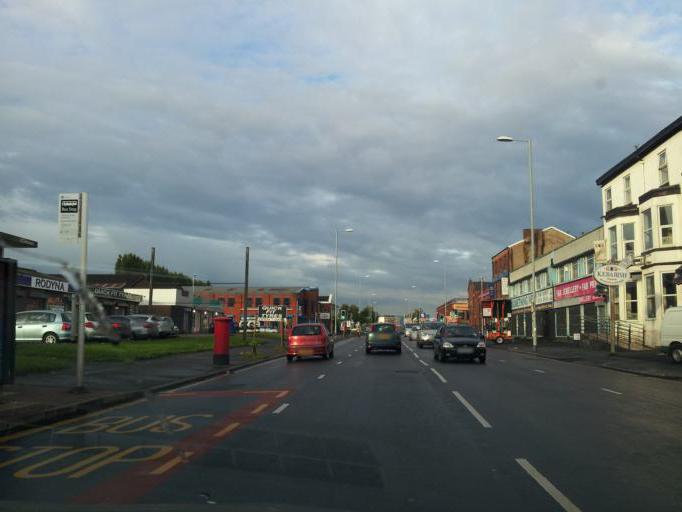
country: GB
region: England
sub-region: Manchester
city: Cheetham Hill
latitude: 53.4947
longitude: -2.2390
